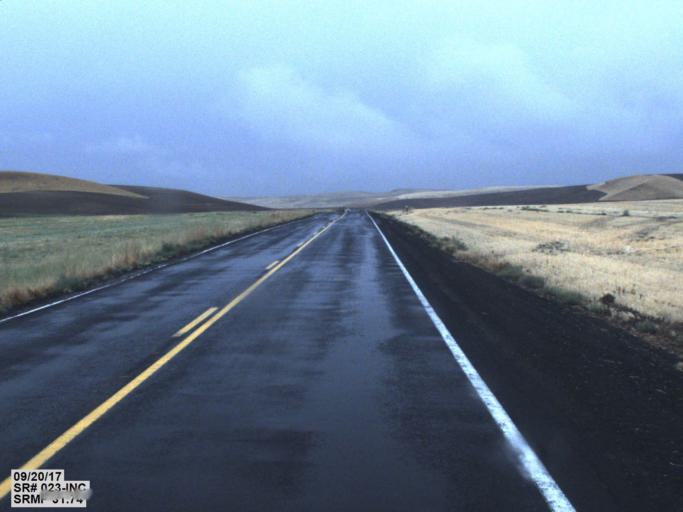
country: US
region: Washington
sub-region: Spokane County
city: Cheney
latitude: 47.1634
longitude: -117.8706
